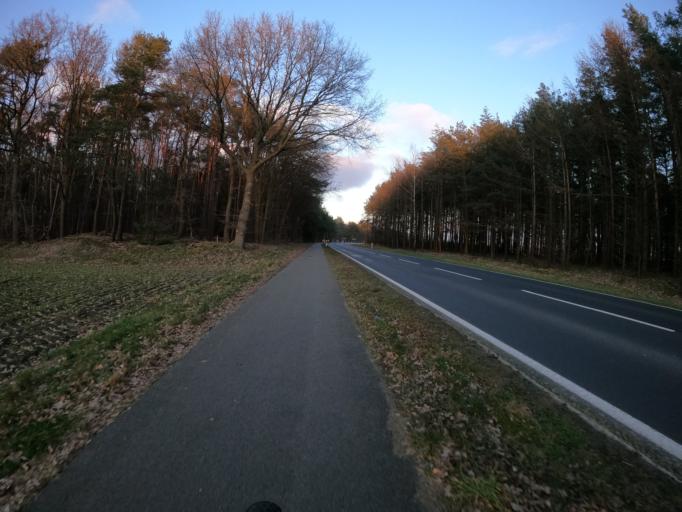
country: DE
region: Lower Saxony
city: Bawinkel
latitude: 52.6660
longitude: 7.4031
